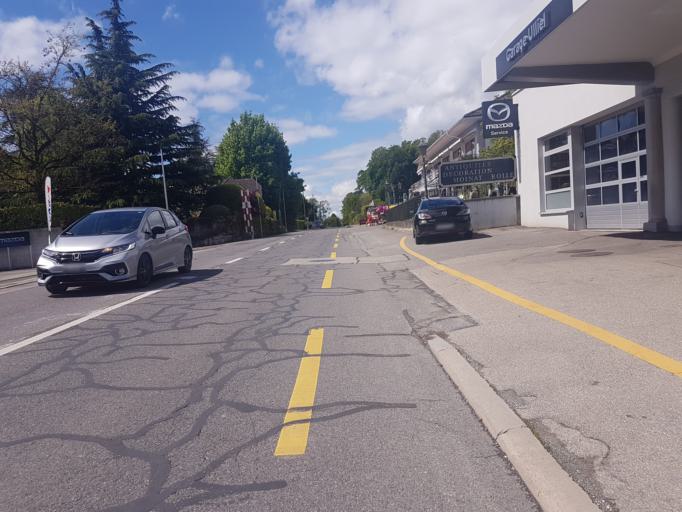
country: CH
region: Vaud
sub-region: Nyon District
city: Rolle
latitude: 46.4525
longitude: 6.3337
